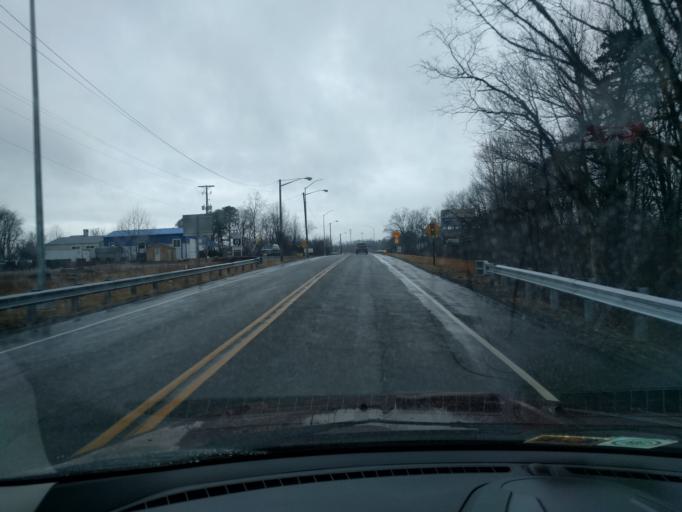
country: US
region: Virginia
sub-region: Pulaski County
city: Pulaski
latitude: 37.0457
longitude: -80.7512
